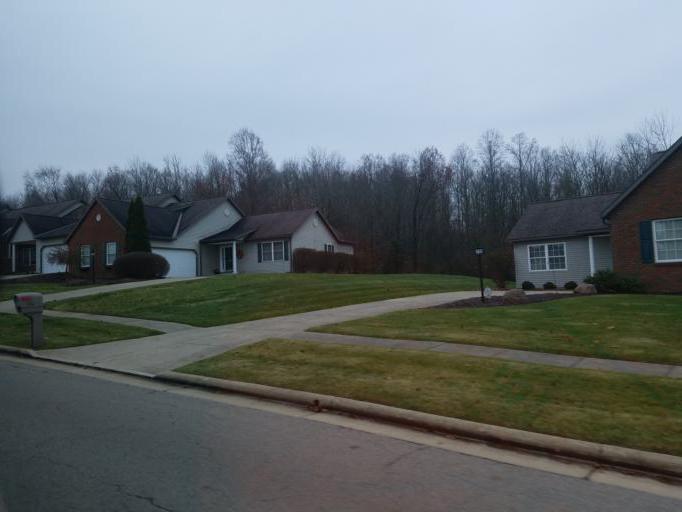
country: US
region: Ohio
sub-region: Richland County
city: Mansfield
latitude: 40.7124
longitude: -82.5279
